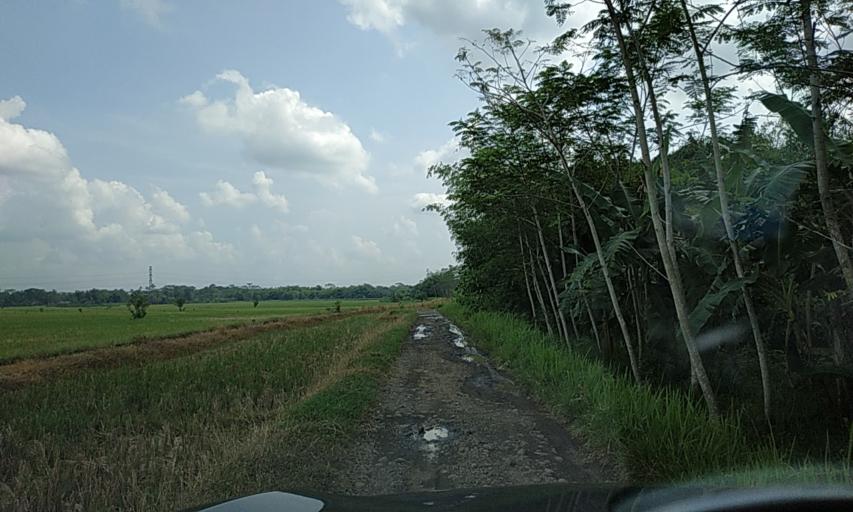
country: ID
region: Central Java
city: Sogati
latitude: -7.3344
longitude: 108.6721
